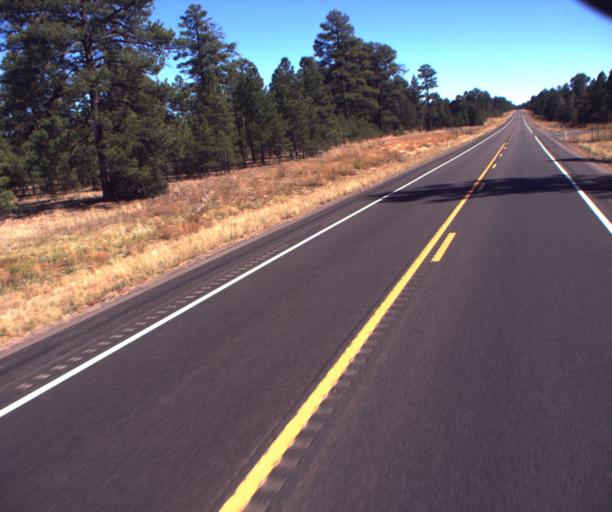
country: US
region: Arizona
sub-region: Apache County
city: Saint Michaels
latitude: 35.6932
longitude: -109.2650
